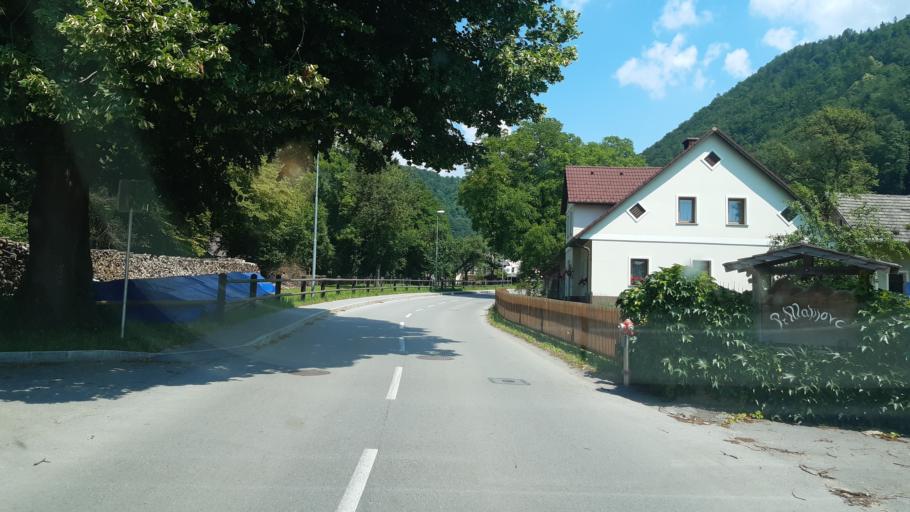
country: SI
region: Cerklje na Gorenjskem
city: Cerklje na Gorenjskem
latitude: 46.2637
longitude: 14.4933
